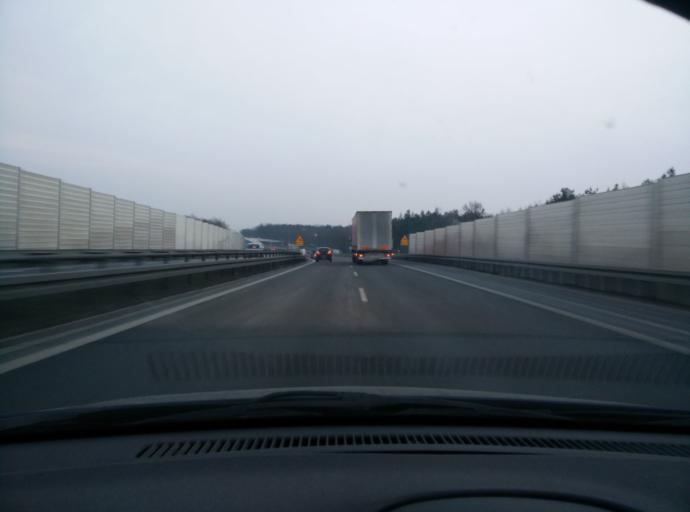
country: PL
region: Greater Poland Voivodeship
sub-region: Powiat poznanski
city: Kornik
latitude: 52.2998
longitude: 17.0491
